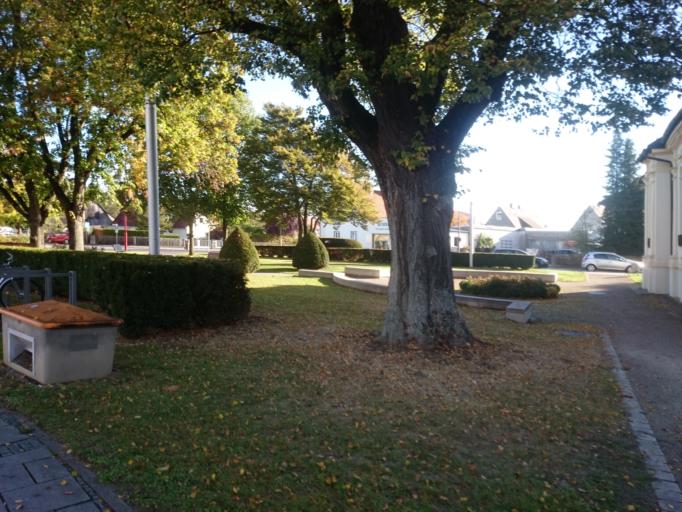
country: DE
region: Bavaria
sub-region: Swabia
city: Gersthofen
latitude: 48.4213
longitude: 10.8792
